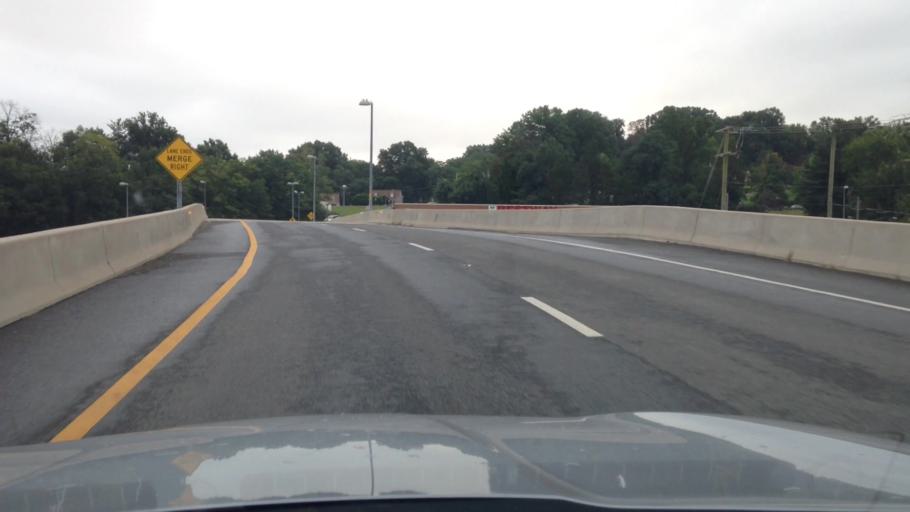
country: US
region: Virginia
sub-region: Fairfax County
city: Huntington
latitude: 38.7981
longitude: -77.0816
